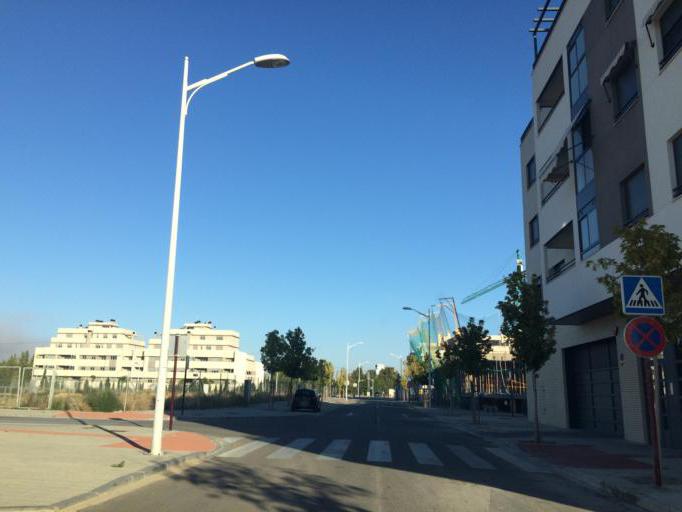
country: ES
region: Castille-La Mancha
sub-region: Provincia de Albacete
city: Albacete
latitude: 39.0048
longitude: -1.8789
